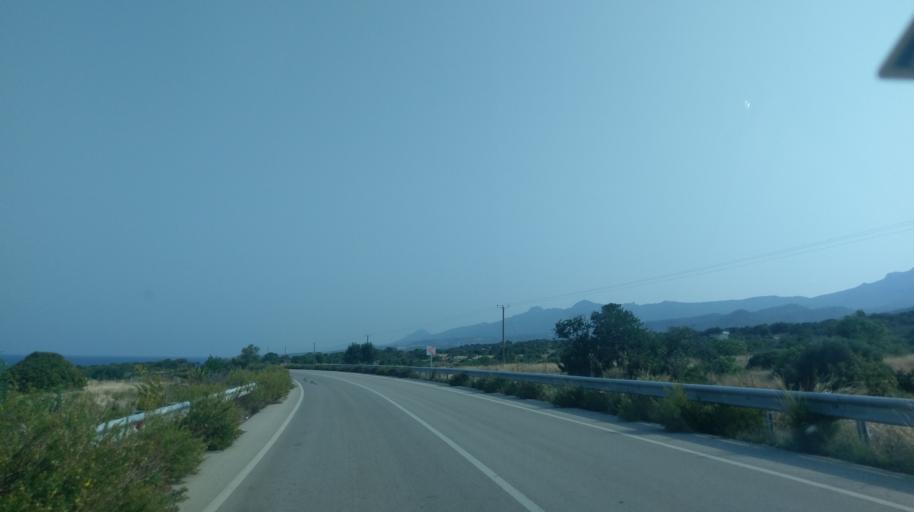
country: CY
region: Ammochostos
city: Trikomo
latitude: 35.4099
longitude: 33.8365
